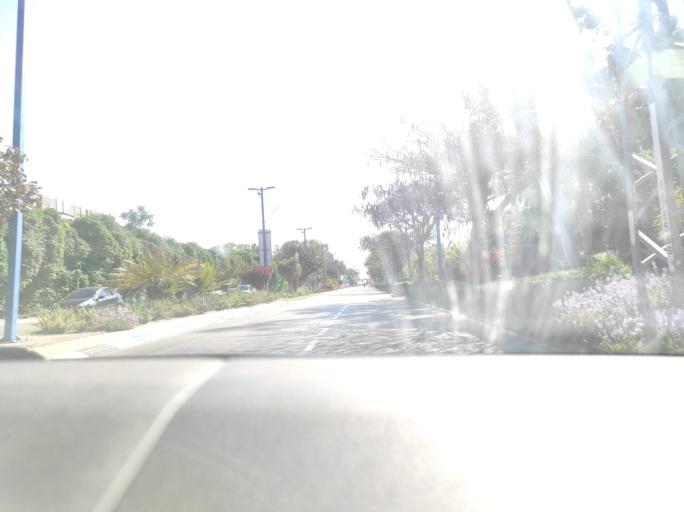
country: IL
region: Southern District
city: Sederot
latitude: 31.5195
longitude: 34.5926
